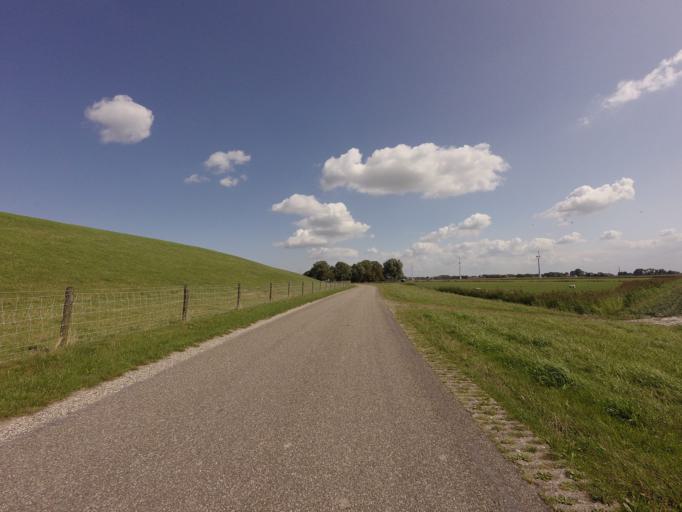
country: NL
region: Friesland
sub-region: Gemeente Ferwerderadiel
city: Hallum
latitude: 53.3249
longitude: 5.7656
